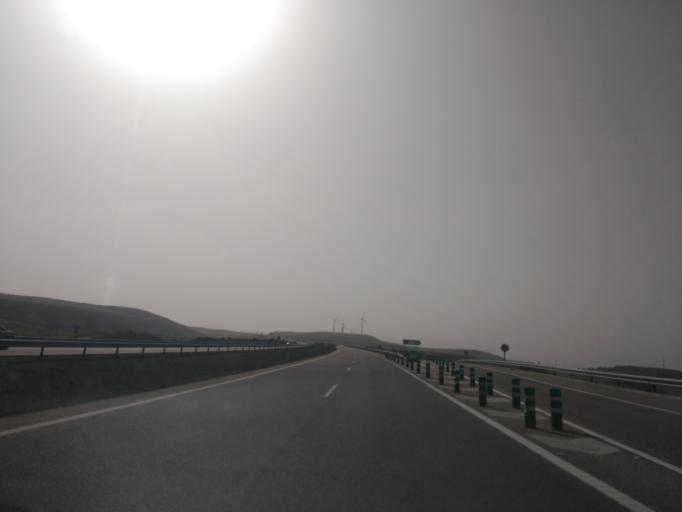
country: ES
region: Castille and Leon
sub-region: Provincia de Palencia
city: Monzon de Campos
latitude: 42.1224
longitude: -4.4799
